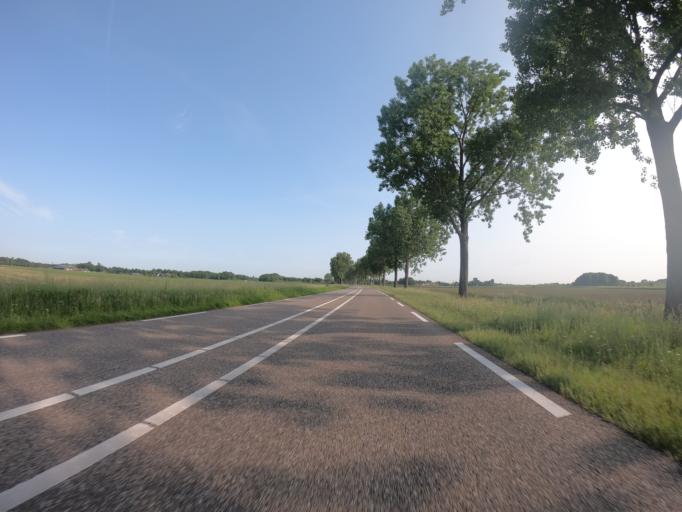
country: NL
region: North Brabant
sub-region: Gemeente Landerd
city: Reek
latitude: 51.7629
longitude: 5.6694
